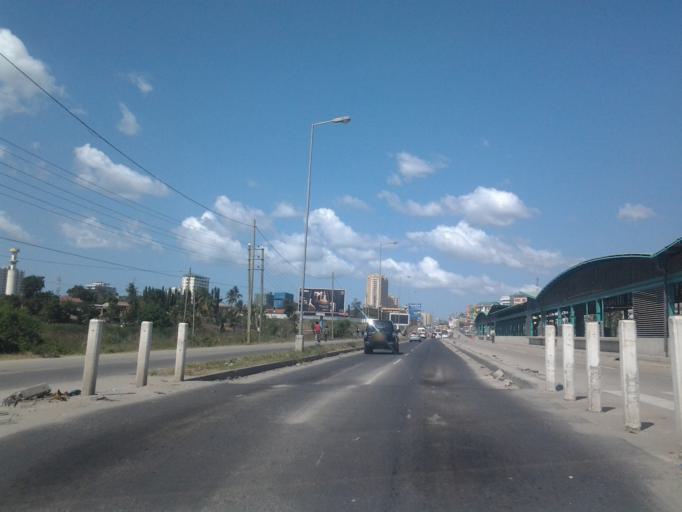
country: TZ
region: Dar es Salaam
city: Dar es Salaam
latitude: -6.8111
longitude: 39.2683
